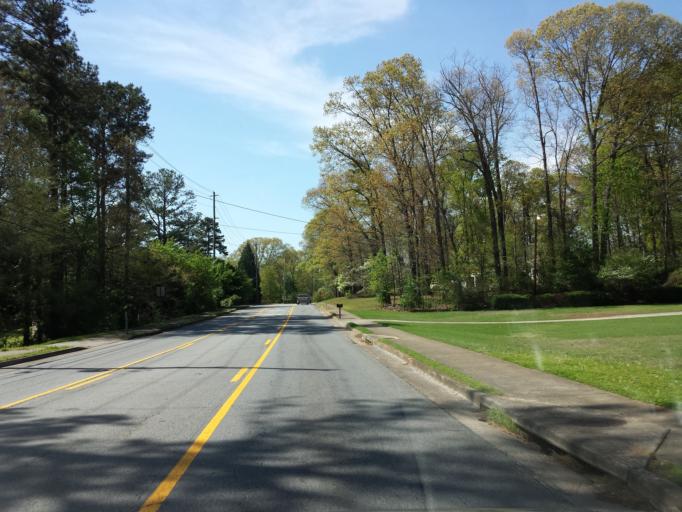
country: US
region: Georgia
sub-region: Cobb County
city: Fair Oaks
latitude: 33.9397
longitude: -84.4917
